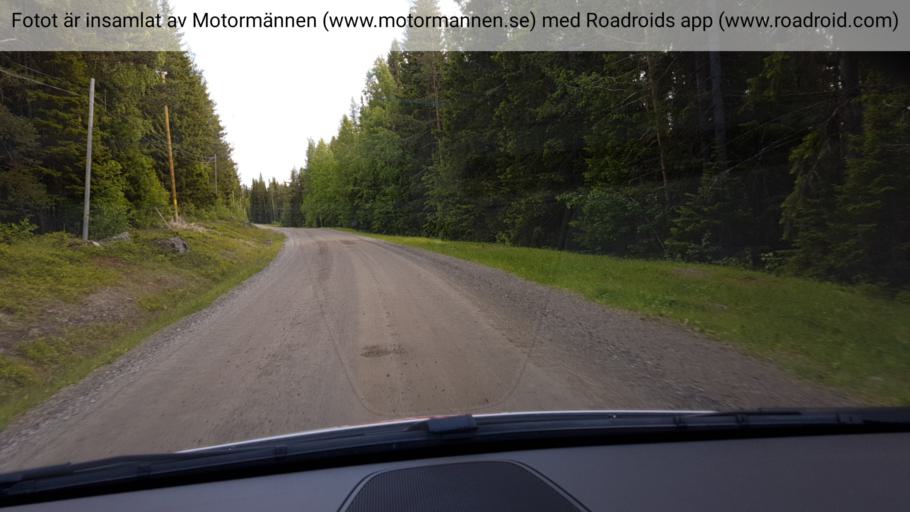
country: SE
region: Vaesterbotten
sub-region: Dorotea Kommun
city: Dorotea
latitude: 64.0866
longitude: 16.5361
